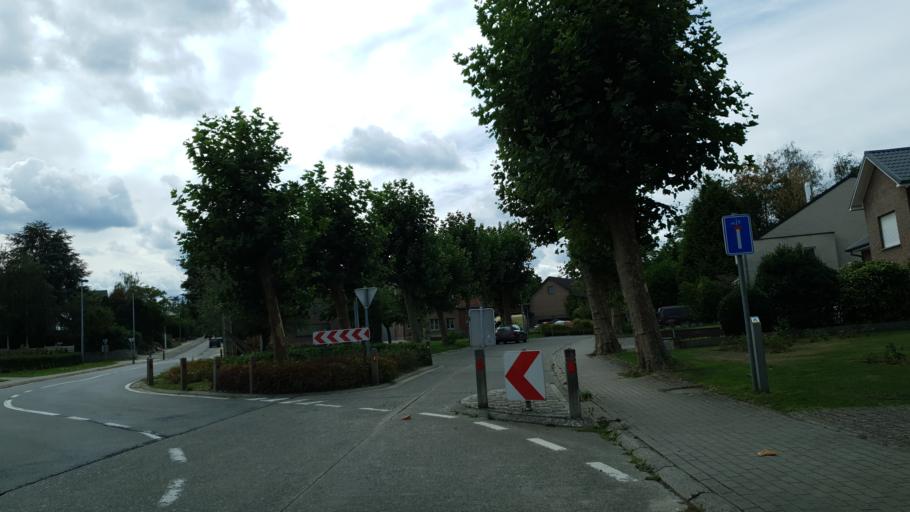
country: BE
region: Flanders
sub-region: Provincie Vlaams-Brabant
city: Herent
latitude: 50.9011
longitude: 4.6851
